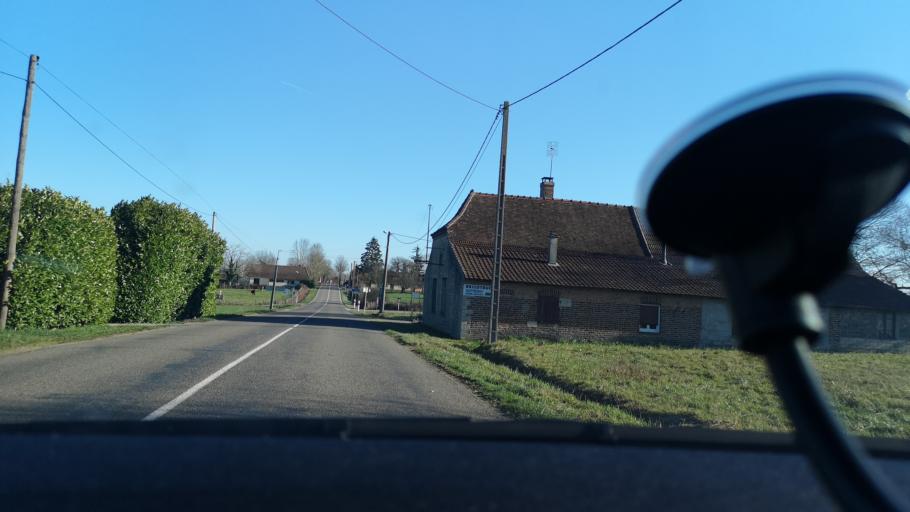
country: FR
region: Franche-Comte
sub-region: Departement du Jura
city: Bletterans
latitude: 46.7433
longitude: 5.3629
